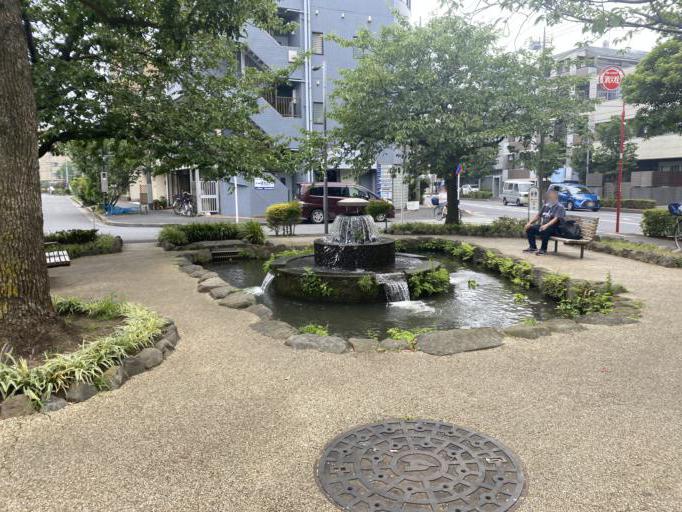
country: JP
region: Tokyo
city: Urayasu
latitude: 35.6960
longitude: 139.9010
